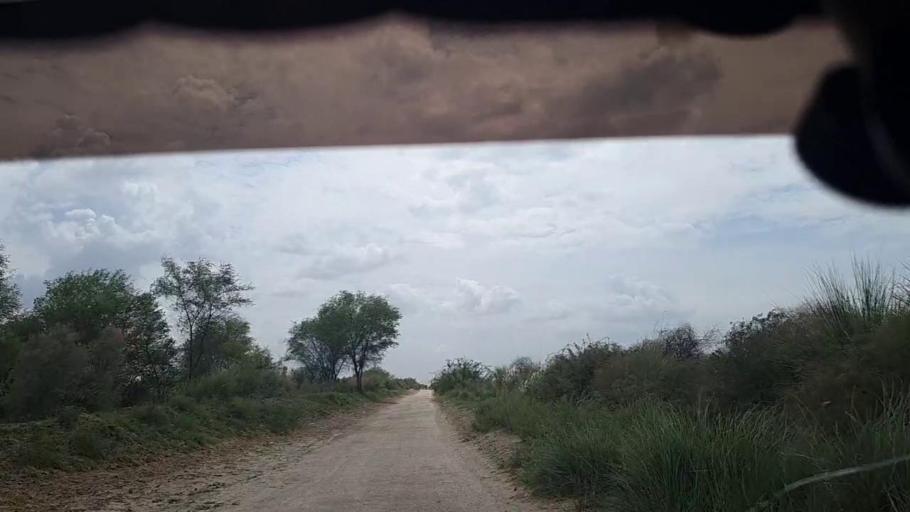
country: PK
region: Sindh
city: Rustam jo Goth
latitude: 28.0349
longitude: 68.9377
